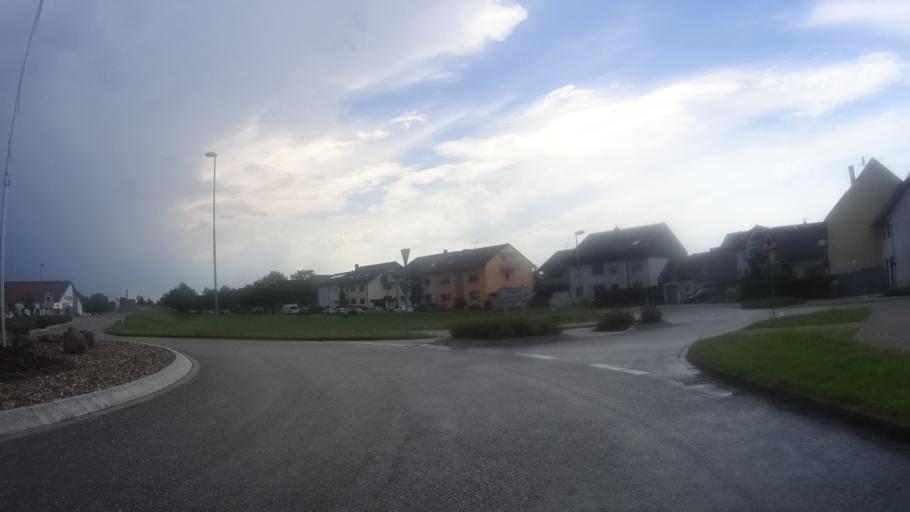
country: DE
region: Baden-Wuerttemberg
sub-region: Karlsruhe Region
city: Bietigheim
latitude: 48.9033
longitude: 8.2505
